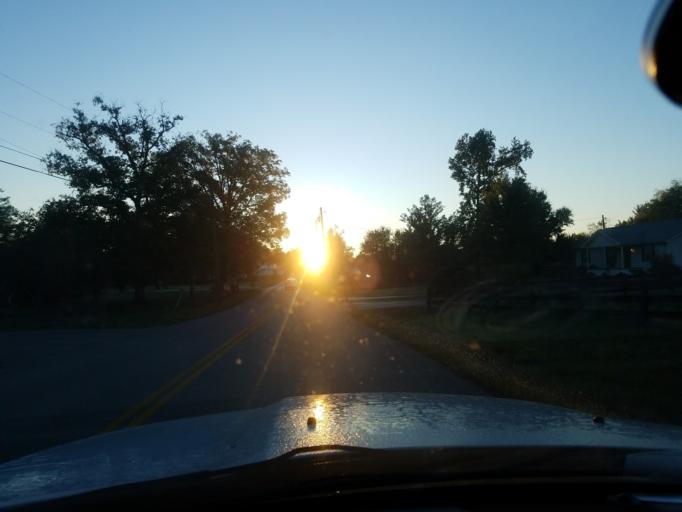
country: US
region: Kentucky
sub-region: Laurel County
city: London
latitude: 37.0966
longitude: -84.0769
